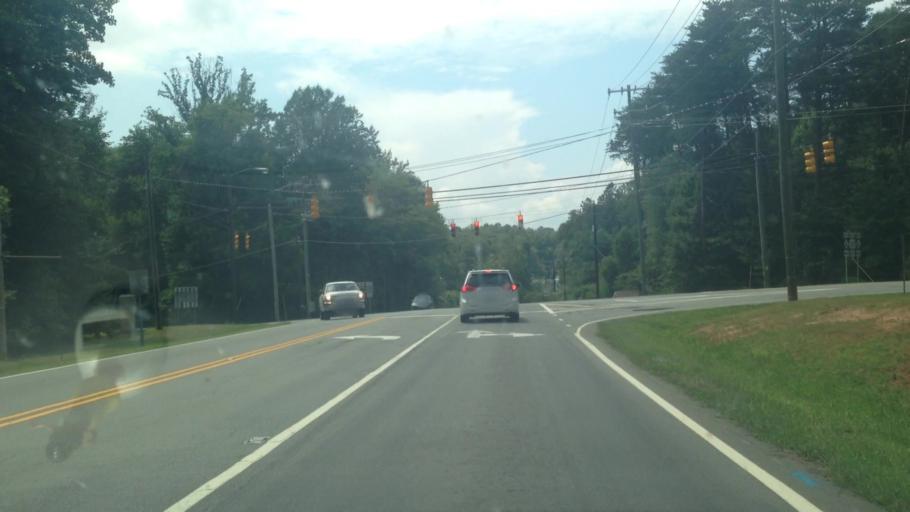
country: US
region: North Carolina
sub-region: Forsyth County
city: Walkertown
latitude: 36.1704
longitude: -80.1601
